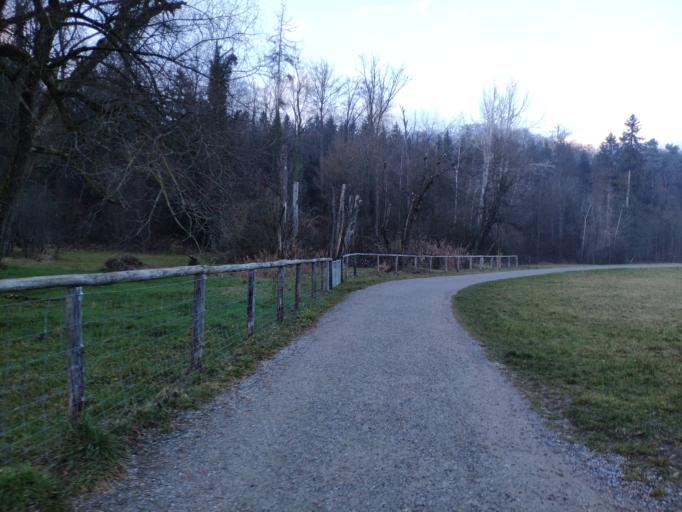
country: CH
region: Zurich
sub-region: Bezirk Zuerich
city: Zuerich (Kreis 3) / Alt-Wiedikon
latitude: 47.3509
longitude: 8.5160
